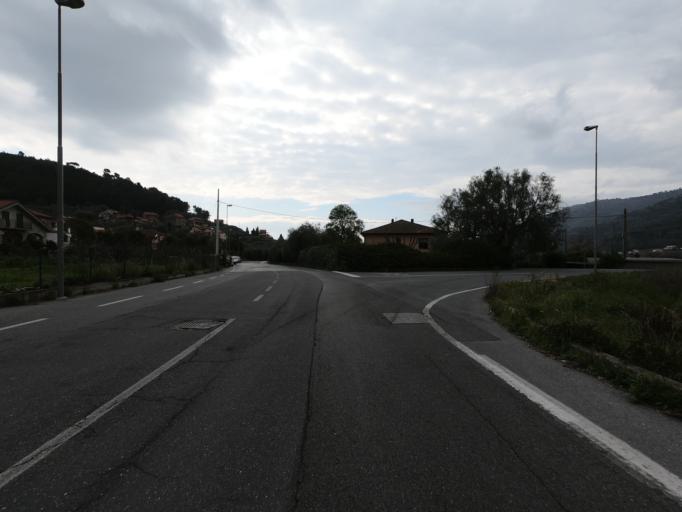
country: IT
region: Liguria
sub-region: Provincia di Savona
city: Laigueglia
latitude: 43.9800
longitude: 8.1349
